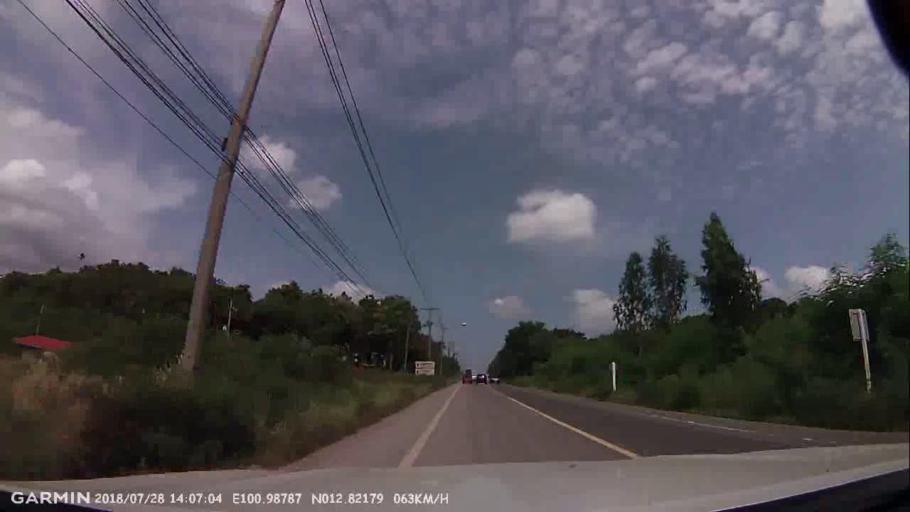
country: TH
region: Rayong
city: Ban Chang
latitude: 12.8217
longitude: 100.9880
